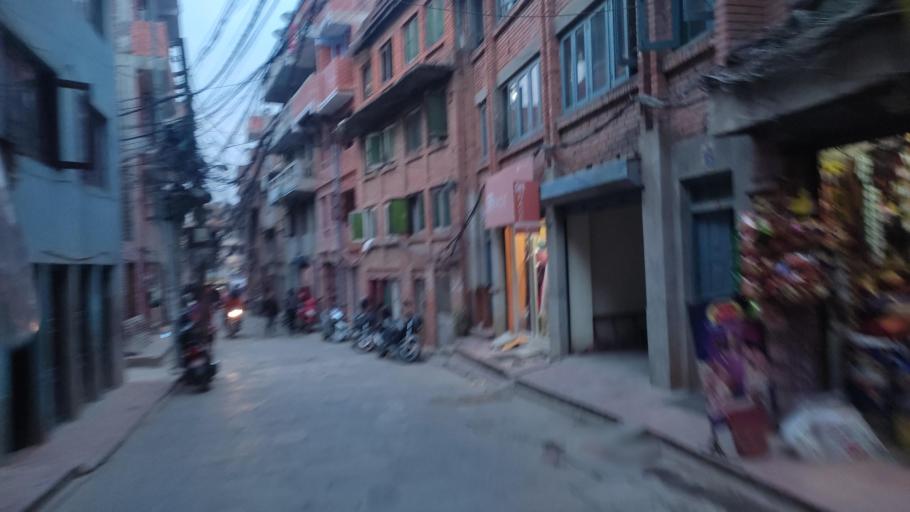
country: NP
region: Central Region
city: Kirtipur
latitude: 27.6700
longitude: 85.2786
